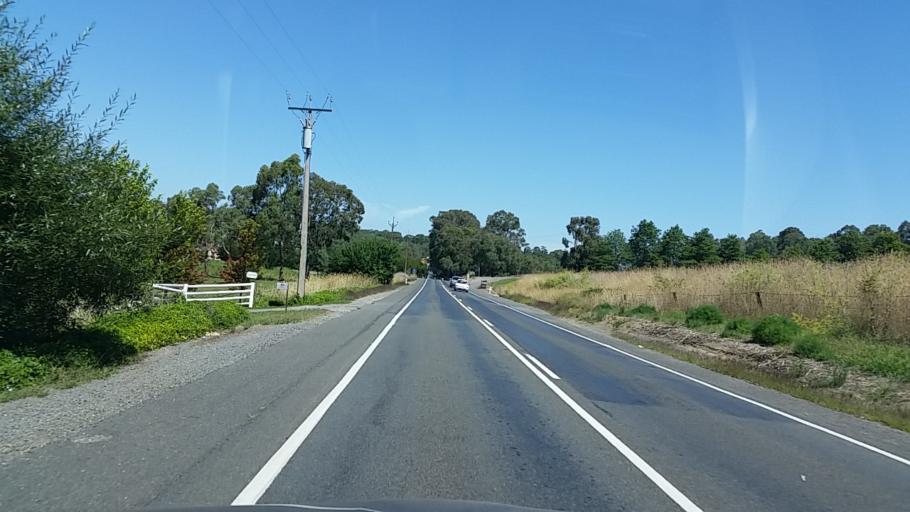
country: AU
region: South Australia
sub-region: Mount Barker
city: Little Hampton
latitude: -35.0412
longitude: 138.8640
